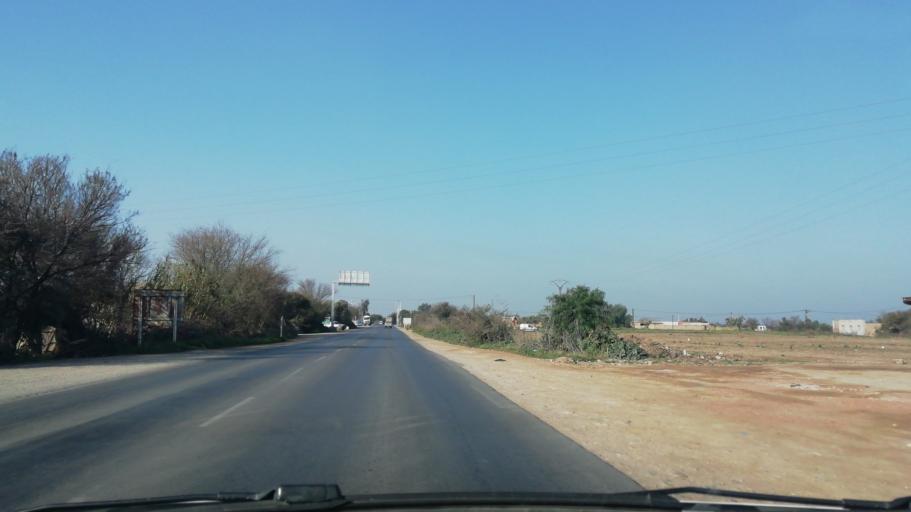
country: DZ
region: Mostaganem
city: Mostaganem
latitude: 35.7517
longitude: 0.1768
